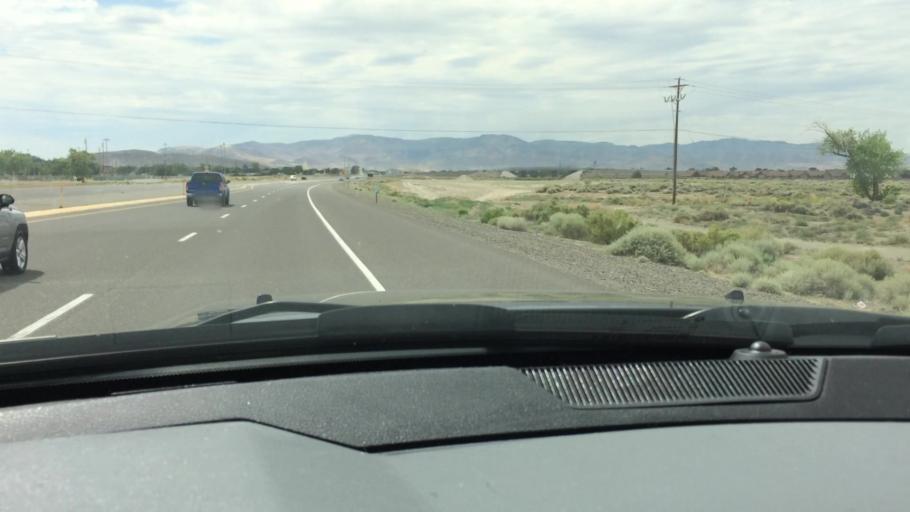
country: US
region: Nevada
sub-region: Lyon County
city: Fernley
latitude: 39.6010
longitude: -119.2167
